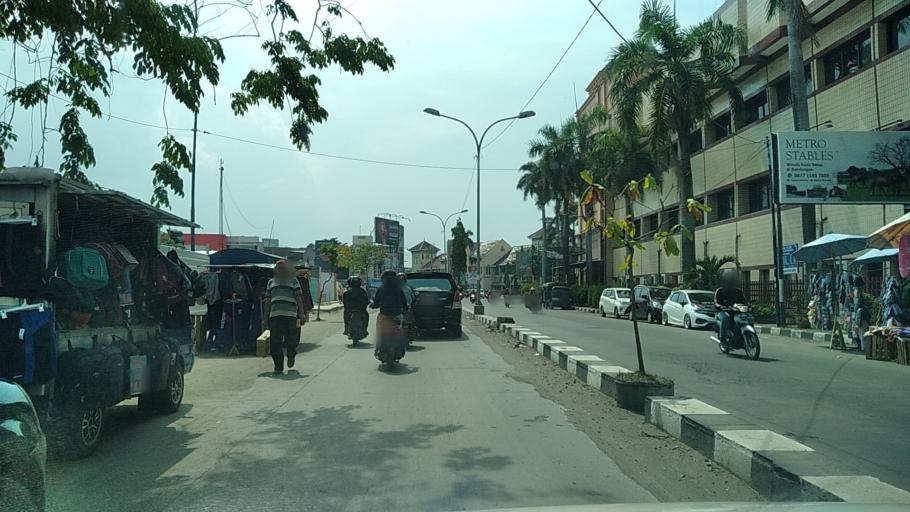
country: ID
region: Central Java
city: Semarang
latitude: -6.9713
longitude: 110.4241
